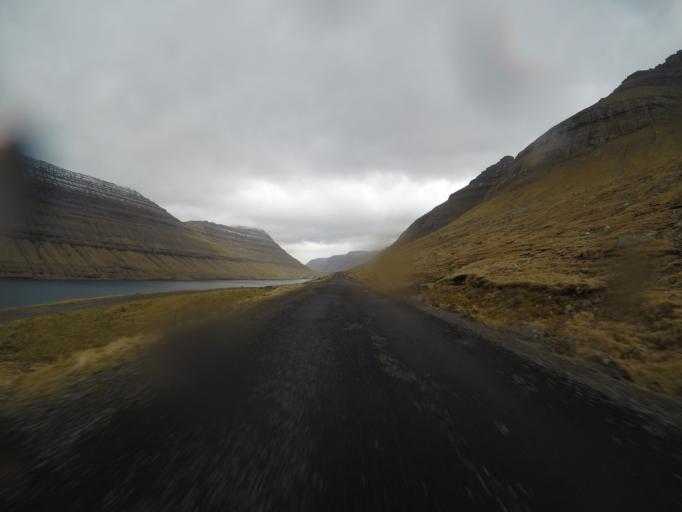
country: FO
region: Nordoyar
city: Klaksvik
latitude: 62.3170
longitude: -6.5556
